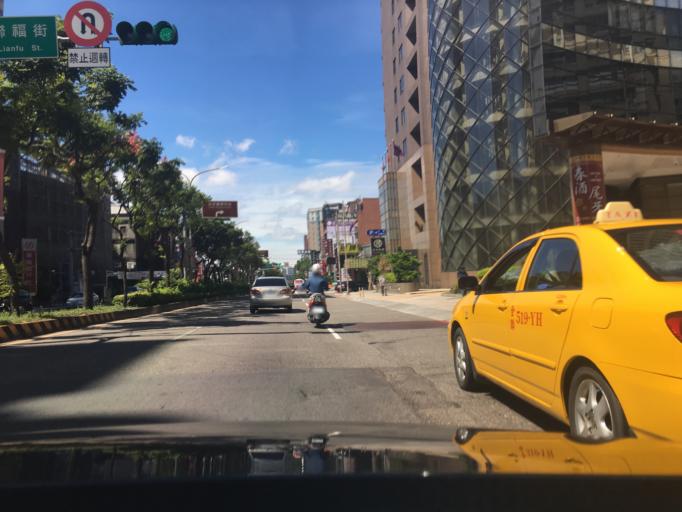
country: TW
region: Taiwan
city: Taoyuan City
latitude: 25.0515
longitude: 121.2886
